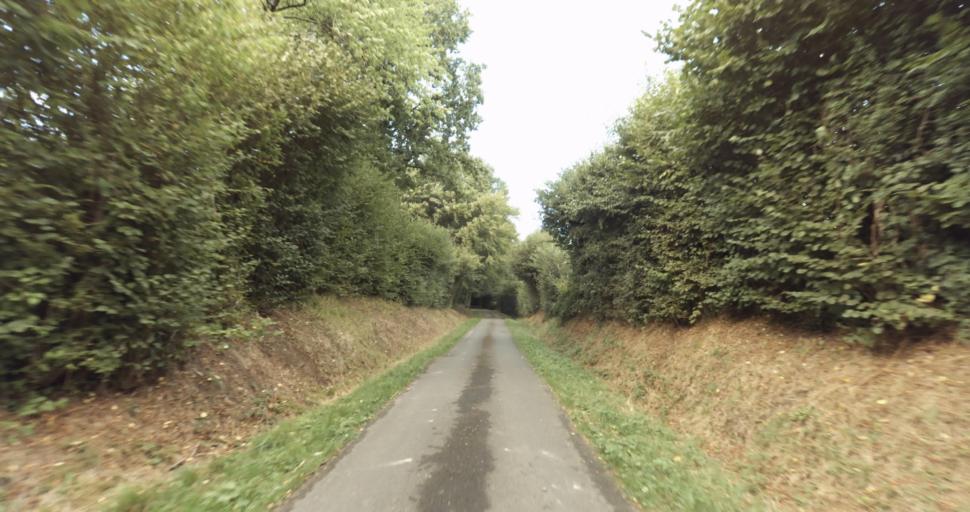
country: FR
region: Lower Normandy
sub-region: Departement de l'Orne
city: Sainte-Gauburge-Sainte-Colombe
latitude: 48.7522
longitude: 0.4127
